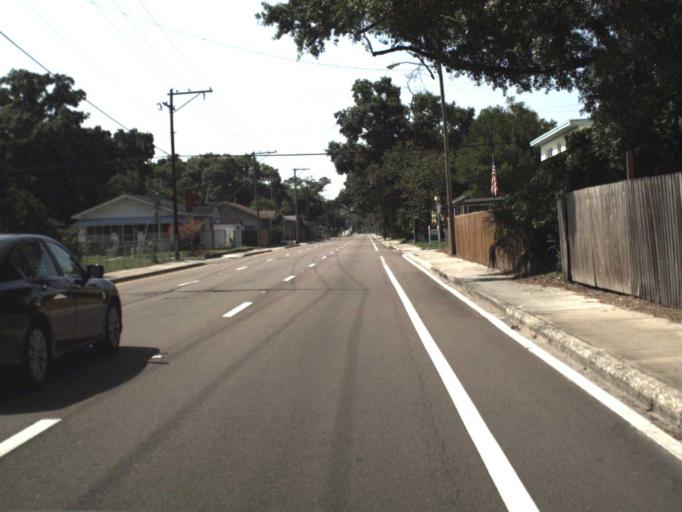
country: US
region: Florida
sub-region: Hillsborough County
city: Tampa
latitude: 27.9858
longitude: -82.4621
